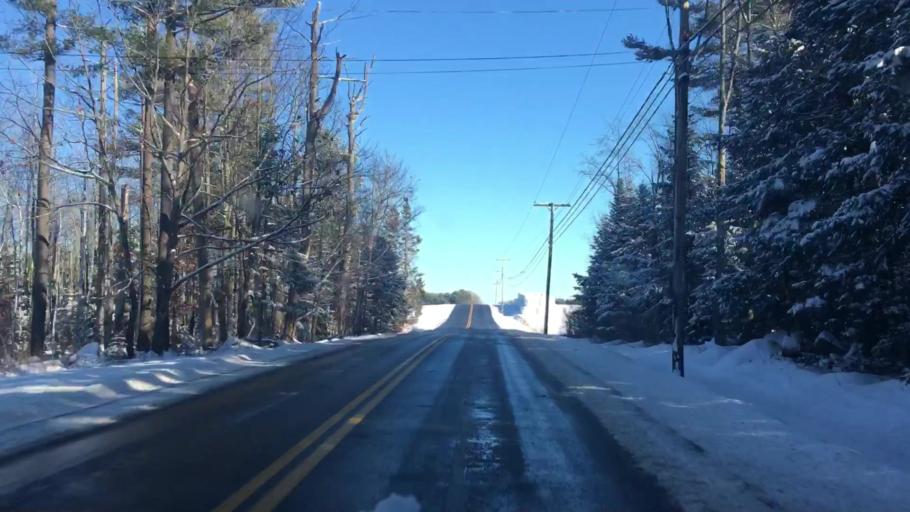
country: US
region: Maine
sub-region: Androscoggin County
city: Lisbon Falls
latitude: 43.9488
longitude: -70.1100
